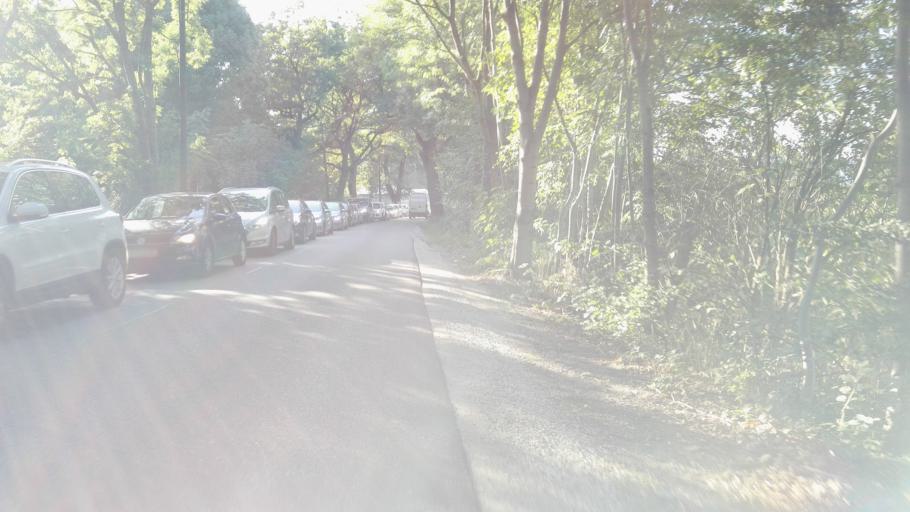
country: AT
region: Styria
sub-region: Politischer Bezirk Graz-Umgebung
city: Feldkirchen bei Graz
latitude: 47.0321
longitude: 15.4365
